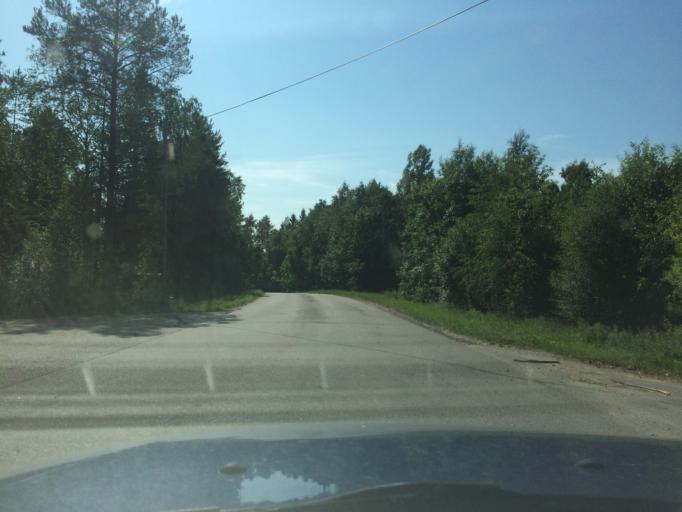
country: SE
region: Norrbotten
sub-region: Pitea Kommun
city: Norrfjarden
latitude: 65.3753
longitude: 21.3914
